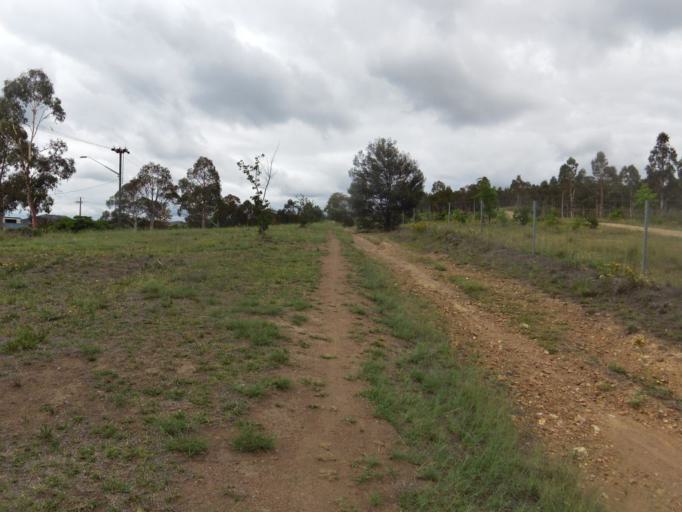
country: AU
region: Australian Capital Territory
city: Macquarie
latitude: -35.3328
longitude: 149.0266
